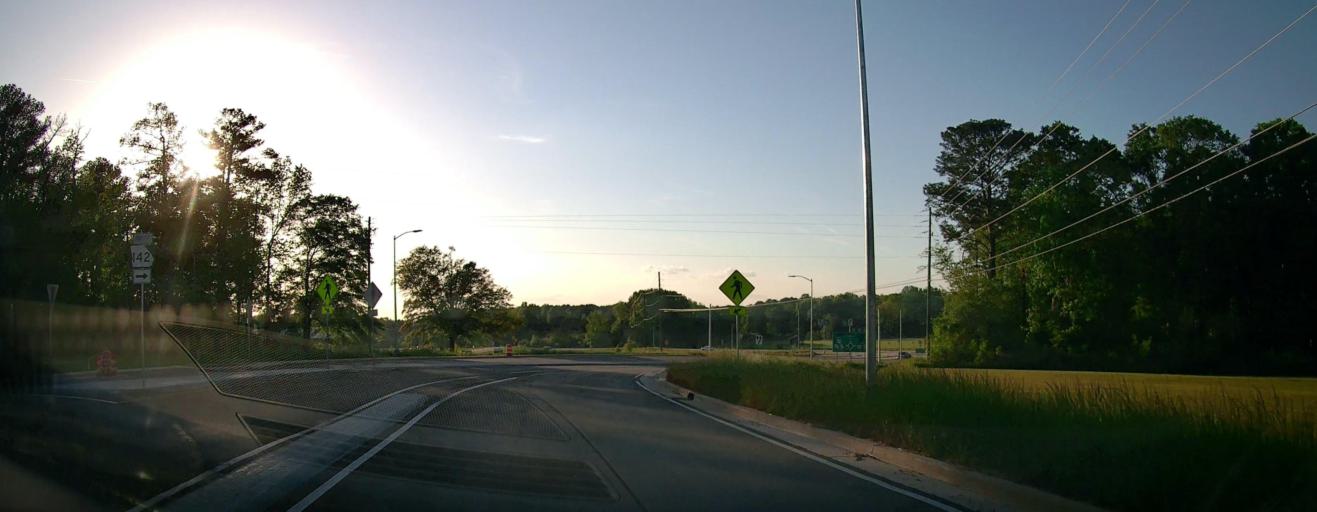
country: US
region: Georgia
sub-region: Newton County
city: Covington
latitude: 33.5907
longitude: -83.7916
